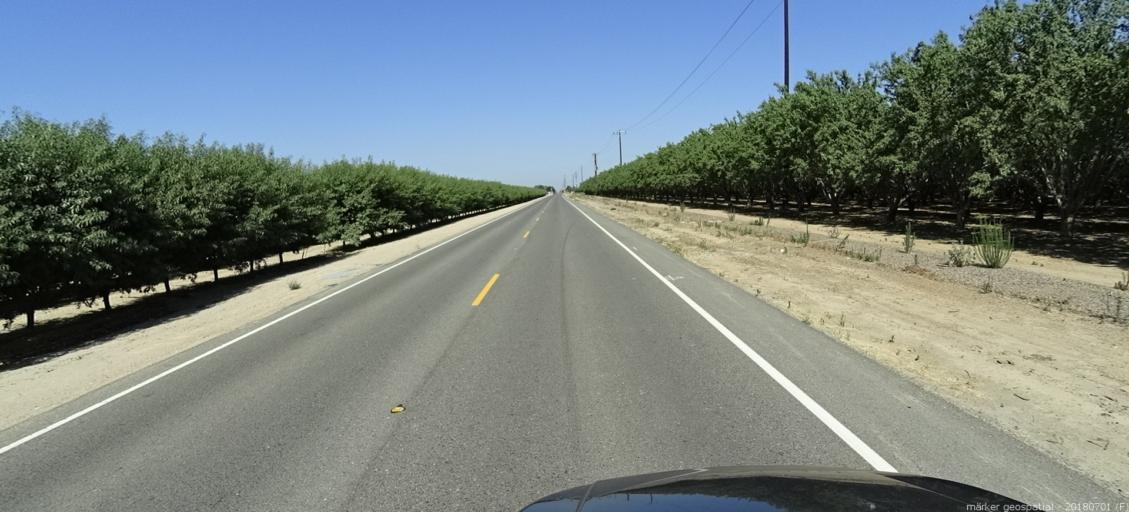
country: US
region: California
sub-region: Madera County
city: Parksdale
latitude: 36.8803
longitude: -119.9301
